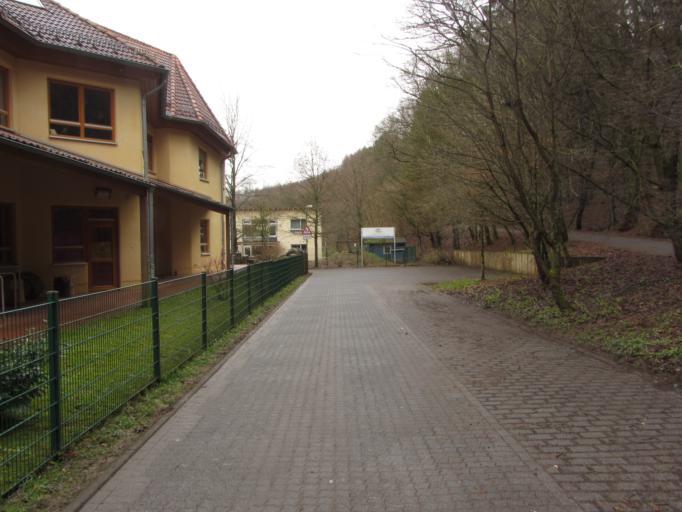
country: DE
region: North Rhine-Westphalia
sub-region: Regierungsbezirk Arnsberg
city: Siegen
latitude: 50.8828
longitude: 8.0032
